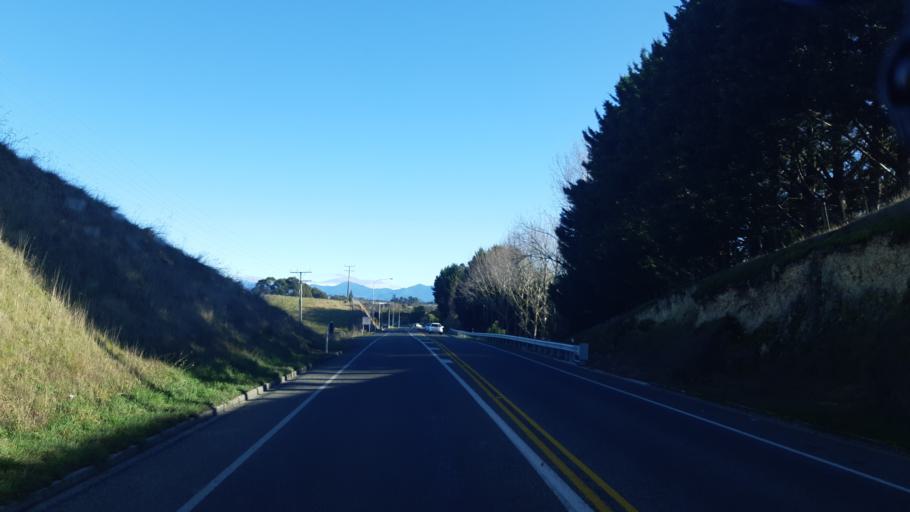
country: NZ
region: Tasman
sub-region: Tasman District
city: Mapua
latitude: -41.2970
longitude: 173.1019
